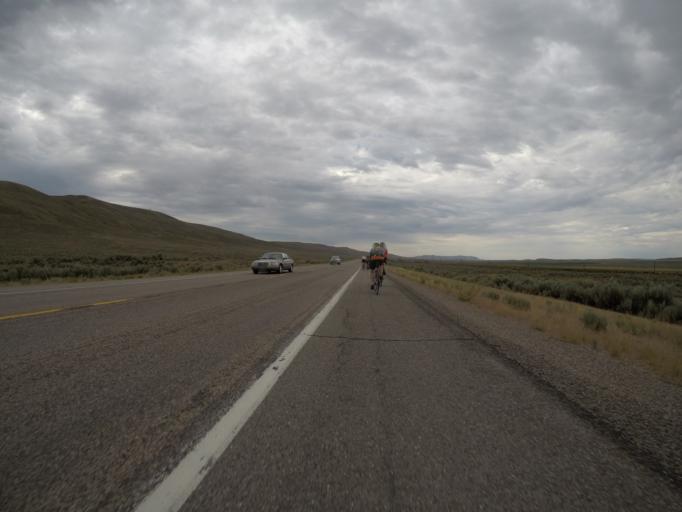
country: US
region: Utah
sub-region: Rich County
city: Randolph
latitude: 41.8569
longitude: -110.9715
